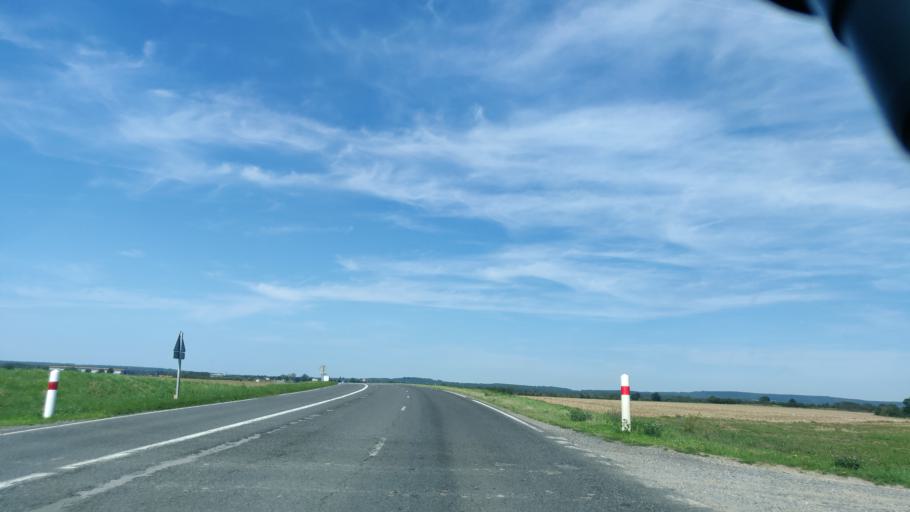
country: FR
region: Picardie
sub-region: Departement de l'Oise
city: Chamant
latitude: 49.1967
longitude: 2.6390
